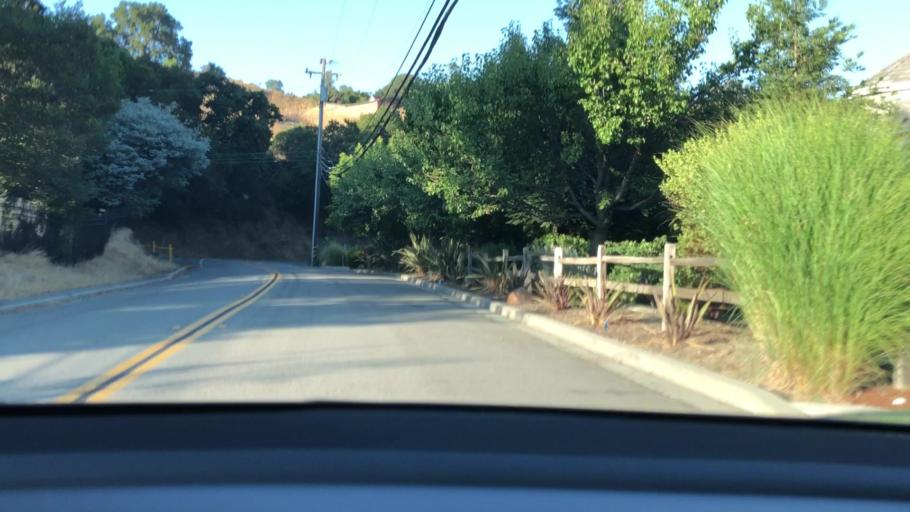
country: US
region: California
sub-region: Santa Clara County
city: Saratoga
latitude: 37.2751
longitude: -122.0665
